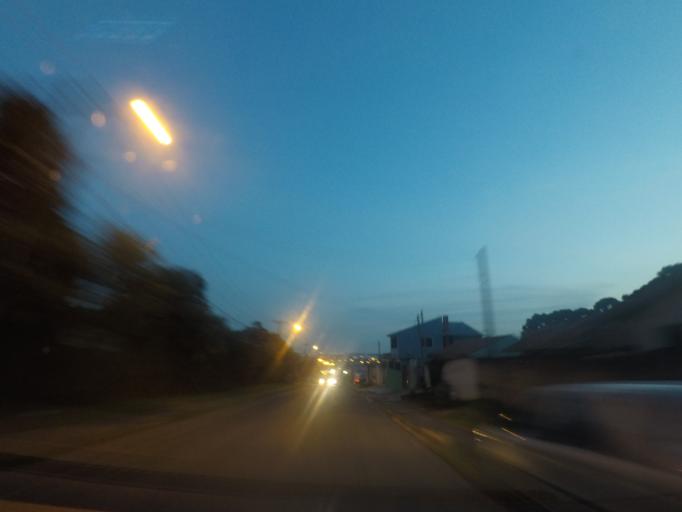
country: BR
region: Parana
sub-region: Pinhais
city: Pinhais
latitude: -25.4678
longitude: -49.1461
